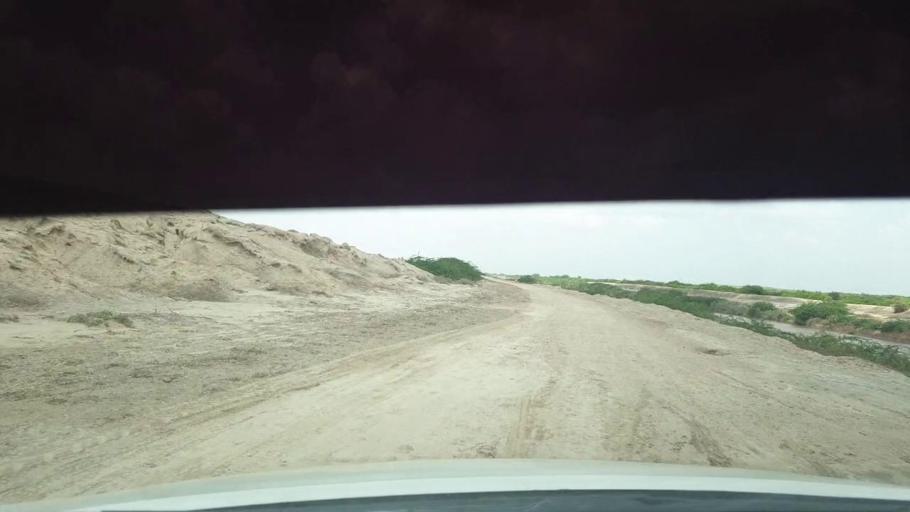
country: PK
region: Sindh
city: Kadhan
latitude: 24.5076
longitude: 69.1183
